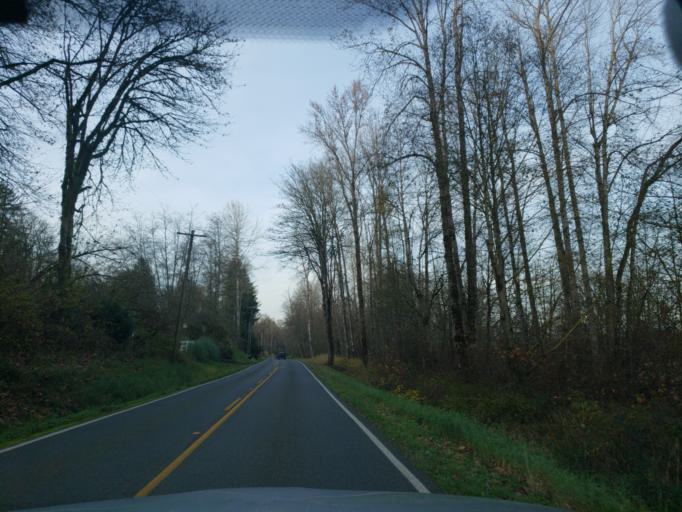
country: US
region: Washington
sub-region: Snohomish County
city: Cathcart
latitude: 47.8537
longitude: -122.0931
